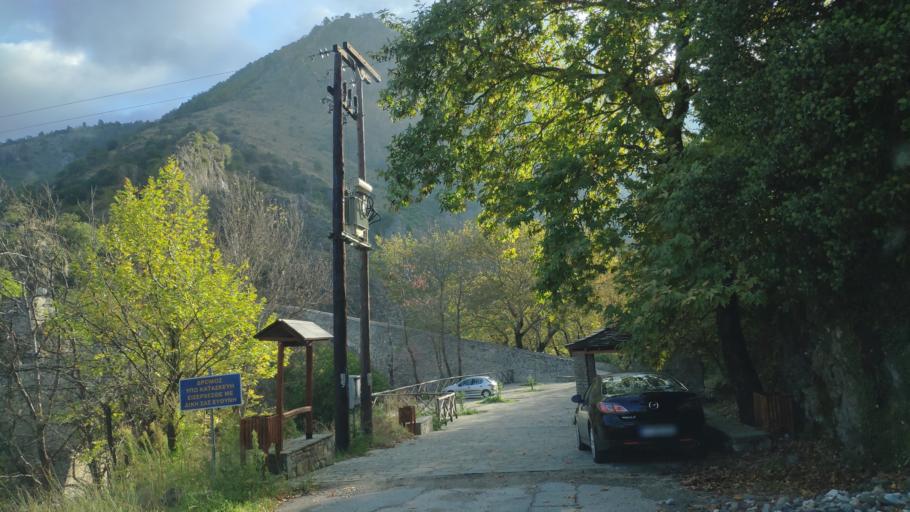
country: GR
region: Epirus
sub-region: Nomos Ioanninon
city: Konitsa
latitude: 40.0361
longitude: 20.7444
